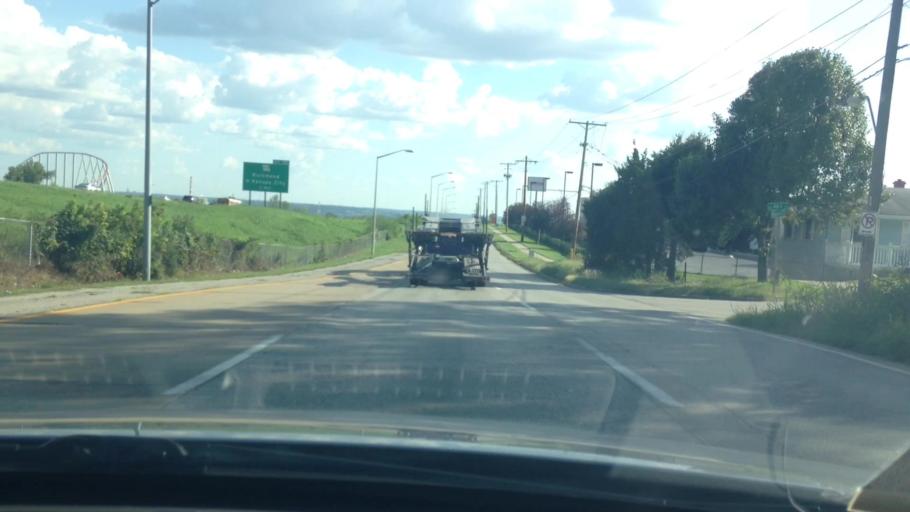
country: US
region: Missouri
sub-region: Clay County
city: Claycomo
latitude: 39.1776
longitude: -94.4937
